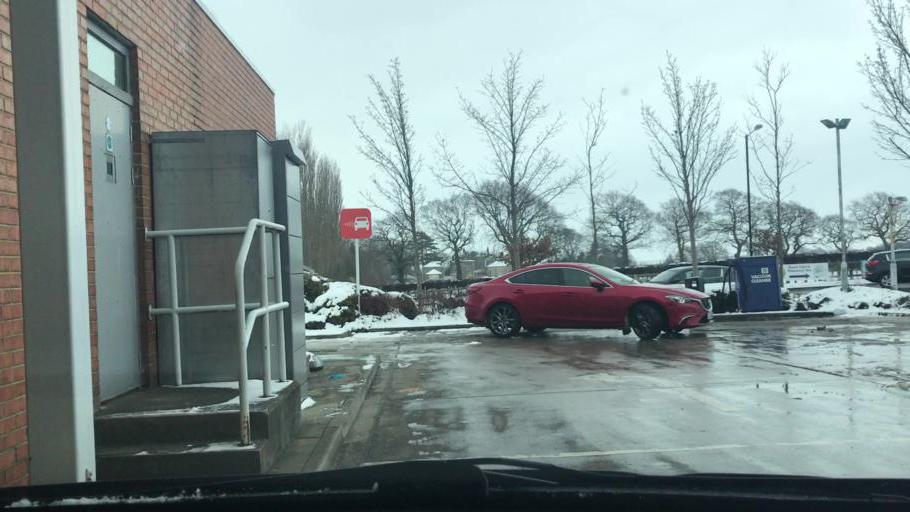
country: GB
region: England
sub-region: North Yorkshire
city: Knaresborough
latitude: 53.9856
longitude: -1.4977
